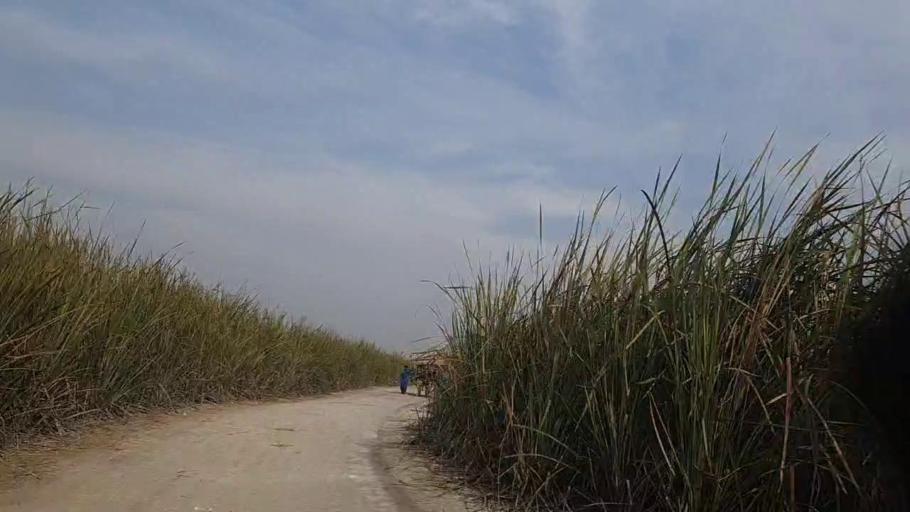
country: PK
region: Sindh
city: Daur
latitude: 26.3709
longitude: 68.2415
